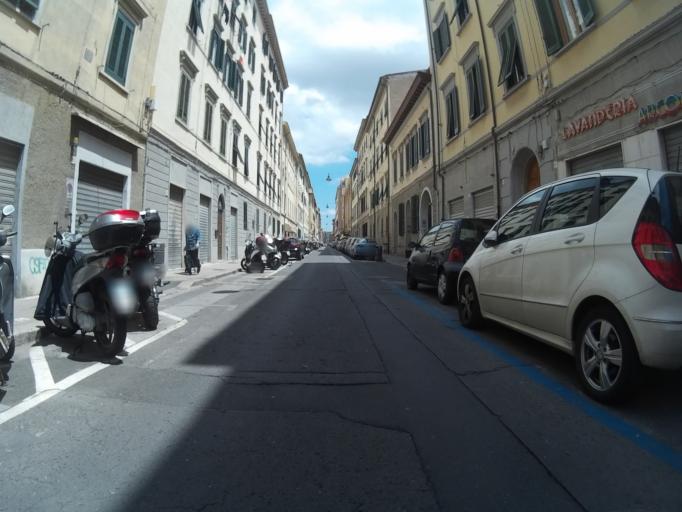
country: IT
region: Tuscany
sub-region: Provincia di Livorno
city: Livorno
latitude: 43.5457
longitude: 10.3084
